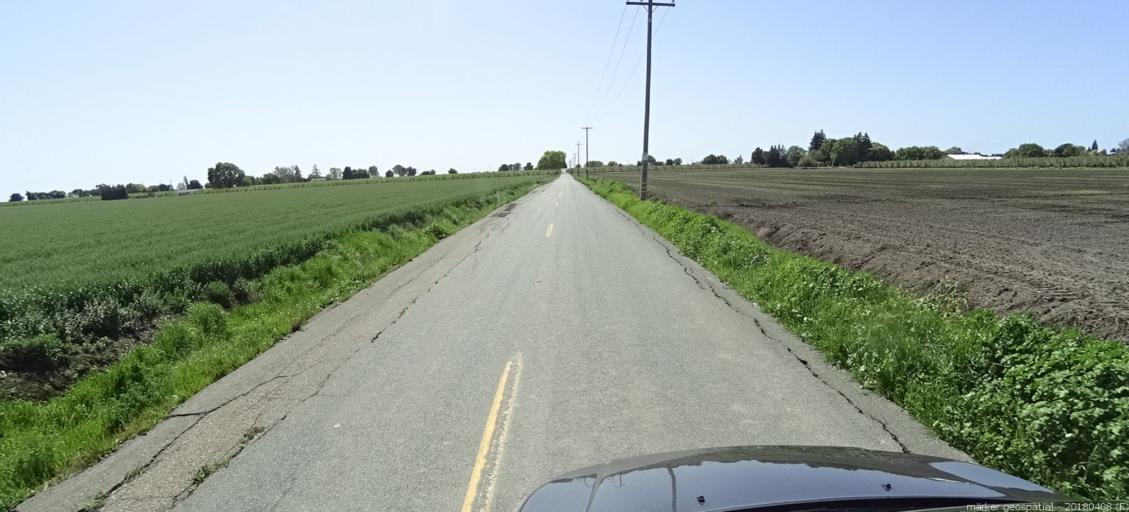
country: US
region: California
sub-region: Sacramento County
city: Walnut Grove
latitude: 38.3033
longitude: -121.5605
